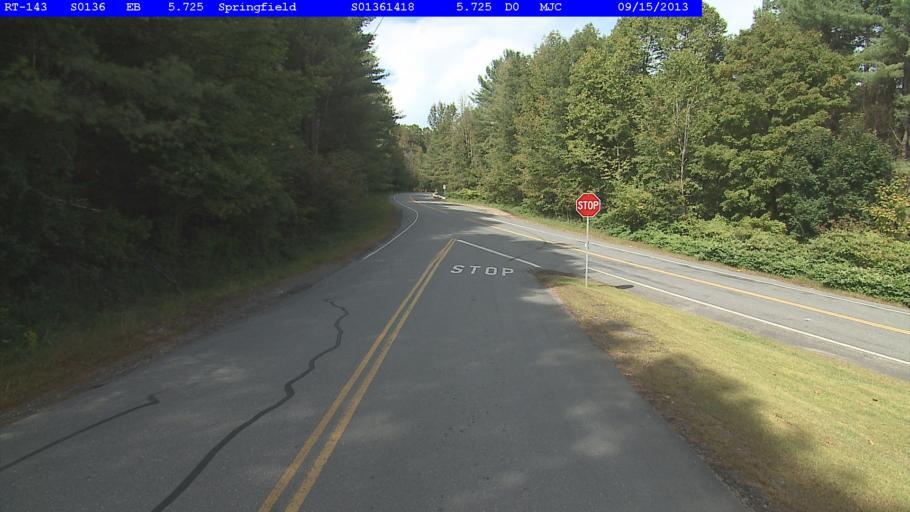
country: US
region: Vermont
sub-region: Windsor County
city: Springfield
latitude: 43.3311
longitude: -72.4122
